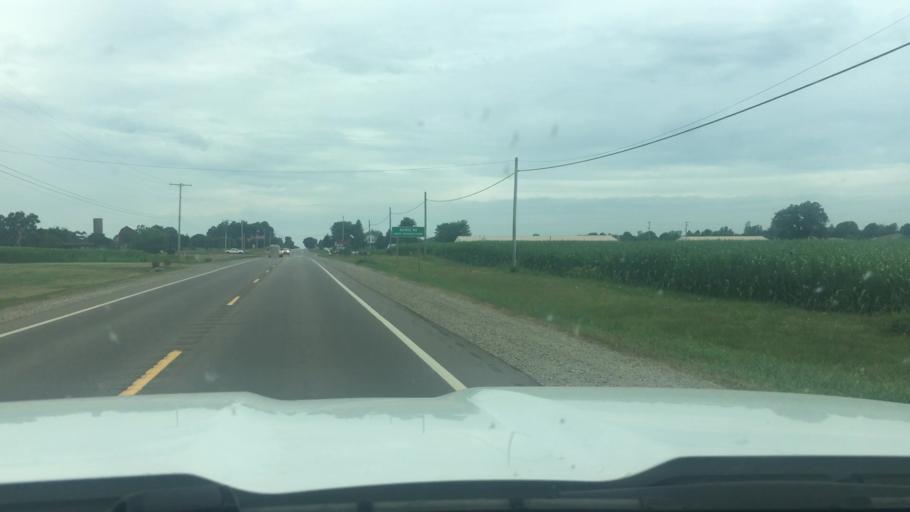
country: US
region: Michigan
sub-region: Clinton County
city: Saint Johns
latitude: 43.0015
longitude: -84.5786
